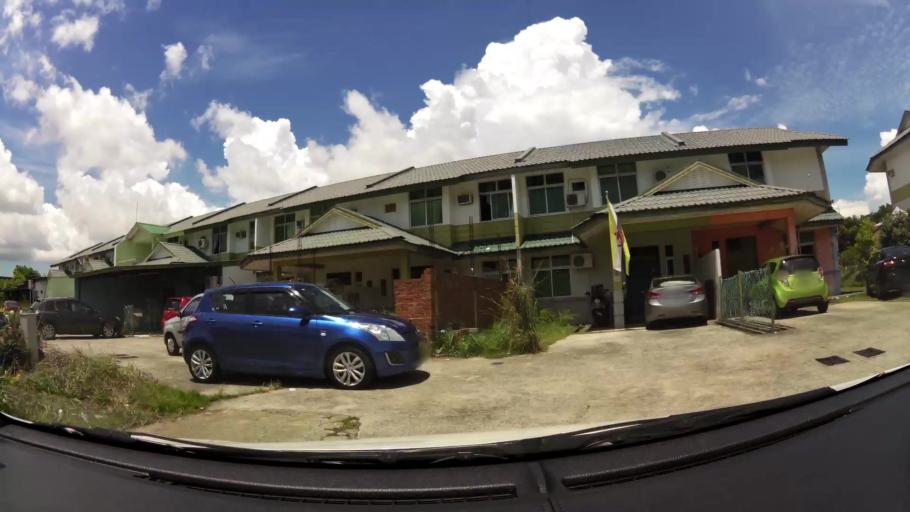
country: BN
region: Brunei and Muara
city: Bandar Seri Begawan
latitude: 4.9694
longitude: 114.9102
